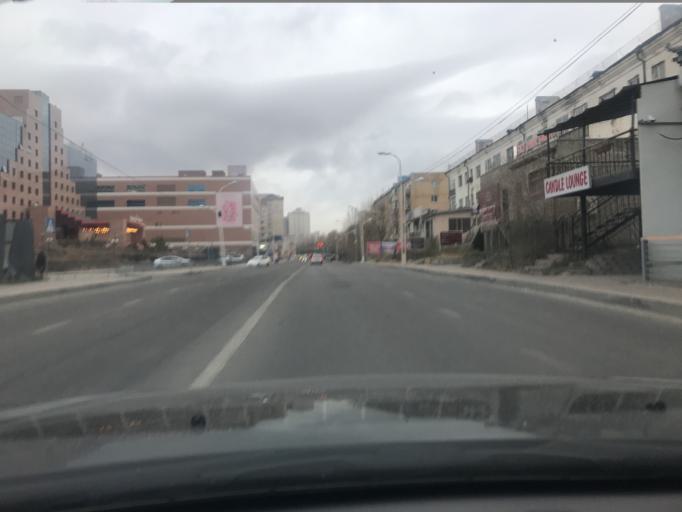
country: MN
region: Ulaanbaatar
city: Ulaanbaatar
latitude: 47.9207
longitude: 106.9351
